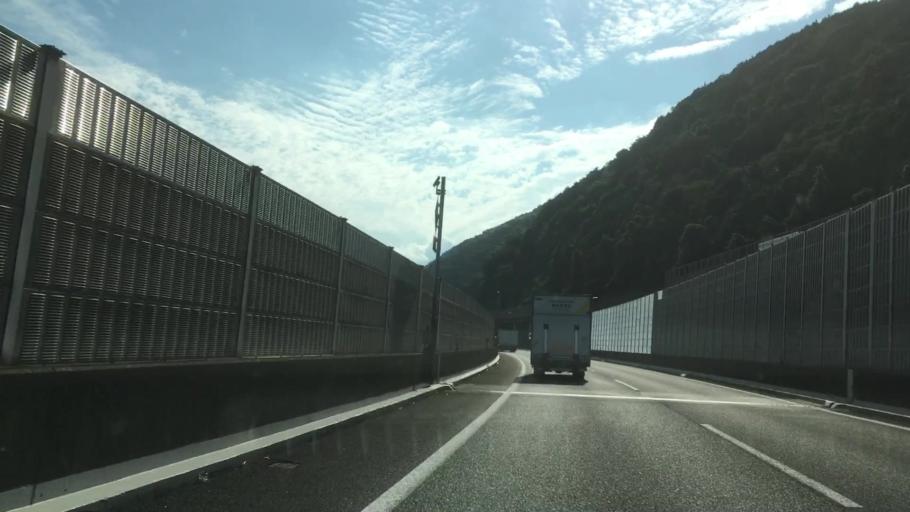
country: JP
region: Yamaguchi
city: Otake
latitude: 34.2243
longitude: 132.2027
